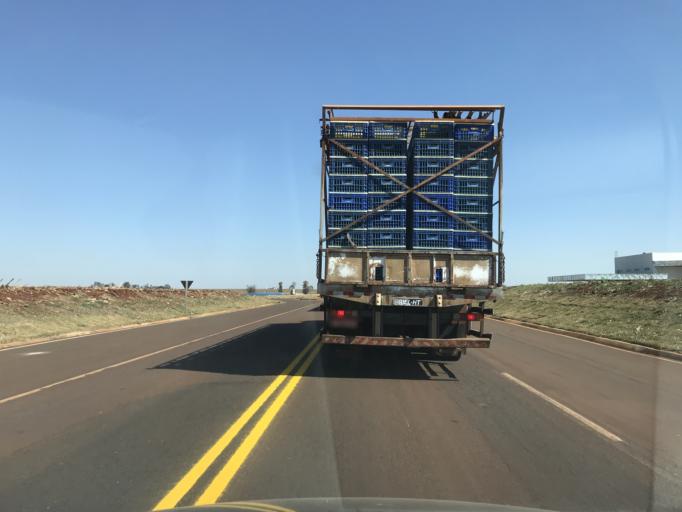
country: BR
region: Parana
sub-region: Palotina
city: Palotina
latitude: -24.4053
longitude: -53.8606
